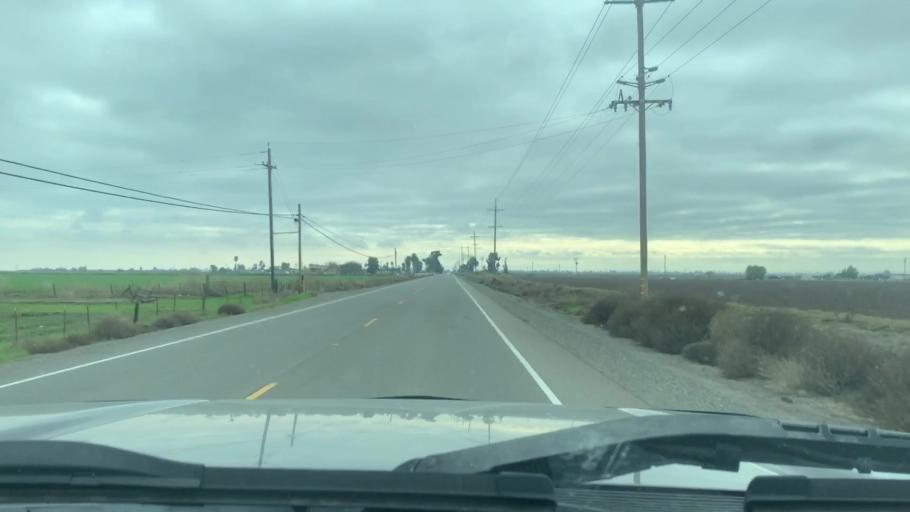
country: US
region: California
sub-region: Merced County
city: Los Banos
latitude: 37.1093
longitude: -120.8349
